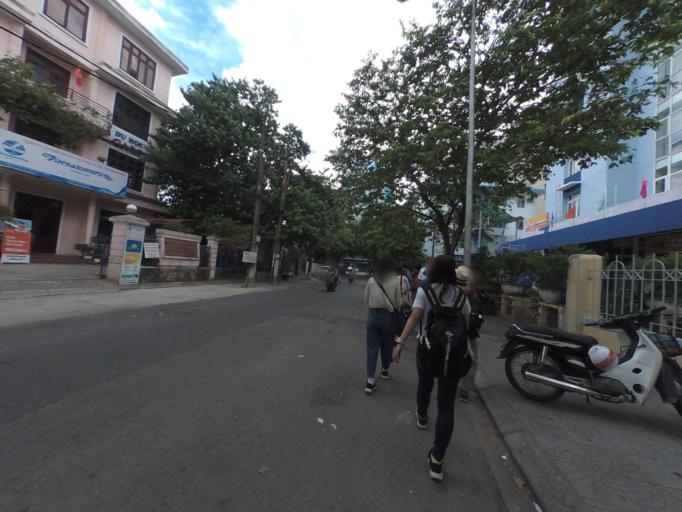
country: VN
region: Thua Thien-Hue
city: Hue
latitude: 16.4616
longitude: 107.5905
